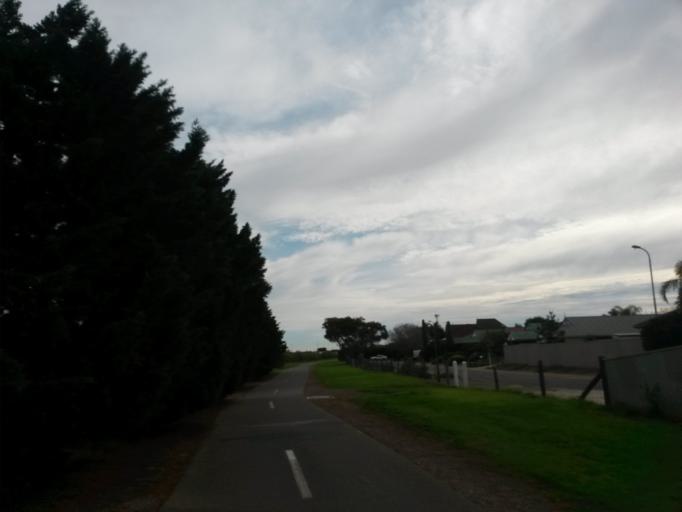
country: AU
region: South Australia
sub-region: Onkaparinga
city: Moana
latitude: -35.1948
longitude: 138.4856
